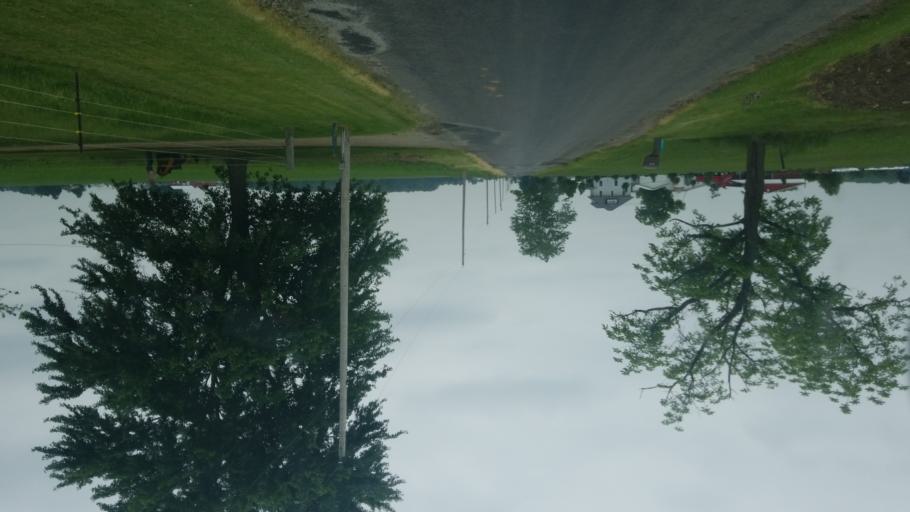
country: US
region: Indiana
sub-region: Elkhart County
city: Wakarusa
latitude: 41.4935
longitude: -86.0696
